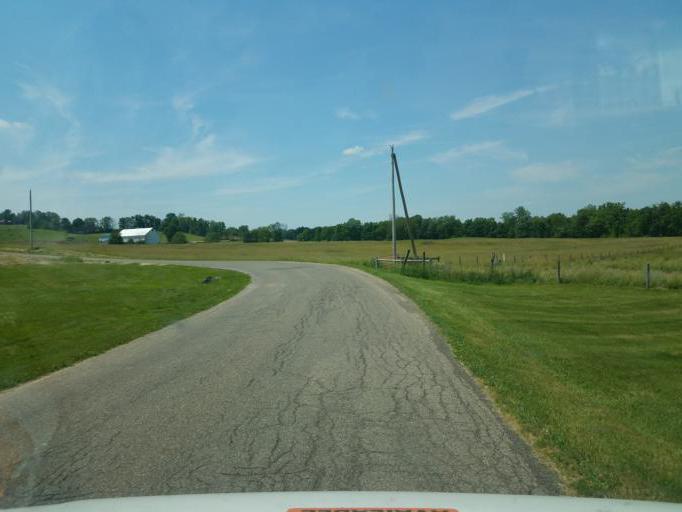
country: US
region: Ohio
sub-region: Knox County
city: Danville
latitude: 40.4960
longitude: -82.2898
